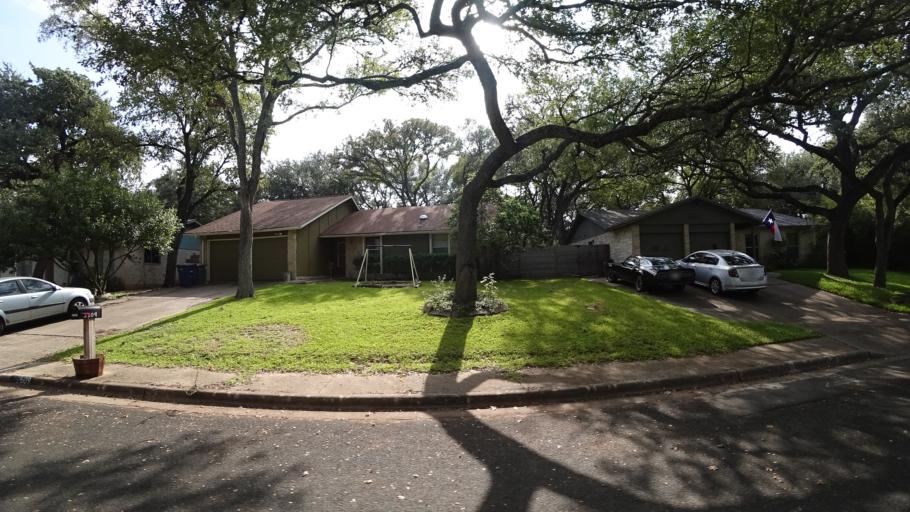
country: US
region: Texas
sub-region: Travis County
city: Shady Hollow
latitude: 30.2008
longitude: -97.8155
